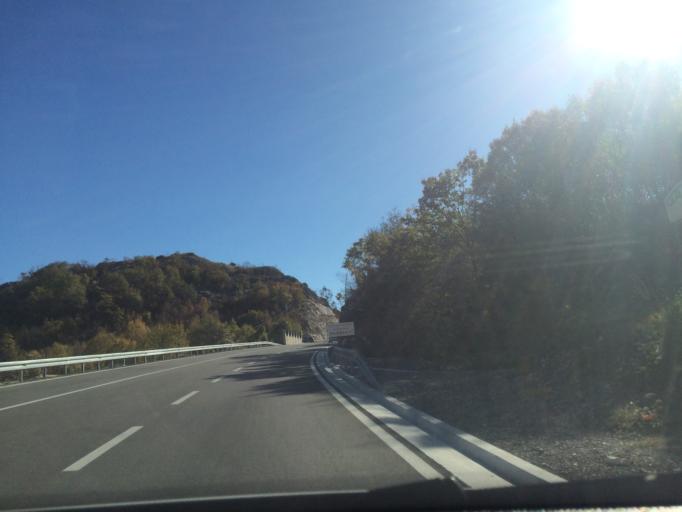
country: ME
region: Cetinje
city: Cetinje
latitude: 42.3883
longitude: 18.9371
